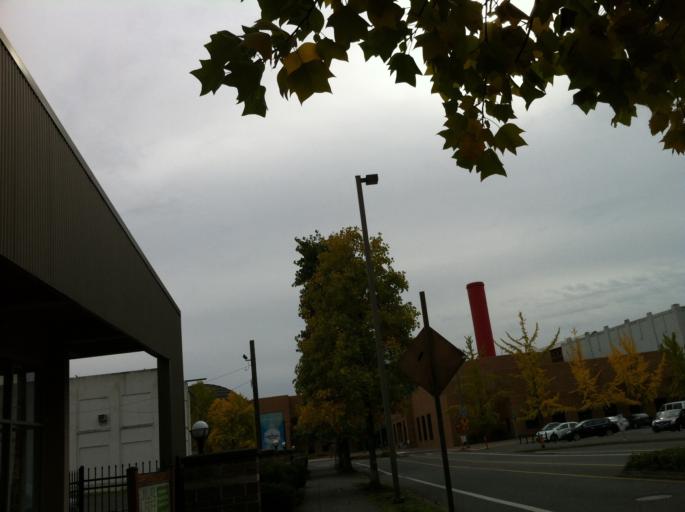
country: US
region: Oregon
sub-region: Multnomah County
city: Portland
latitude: 45.5099
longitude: -122.6658
